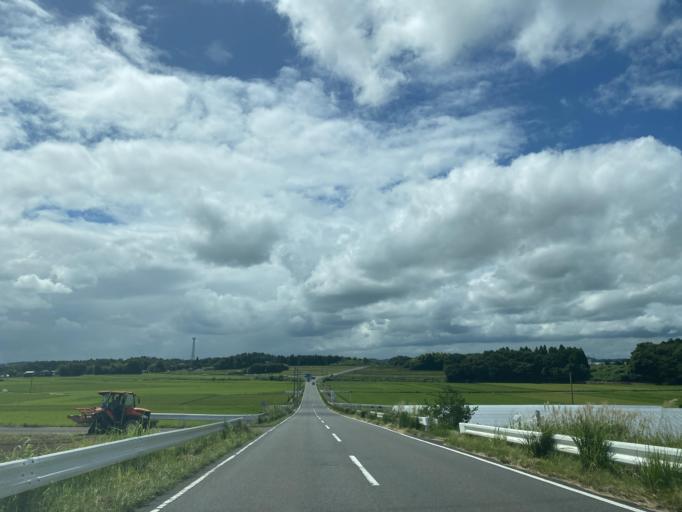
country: JP
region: Fukushima
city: Koriyama
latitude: 37.3724
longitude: 140.2940
